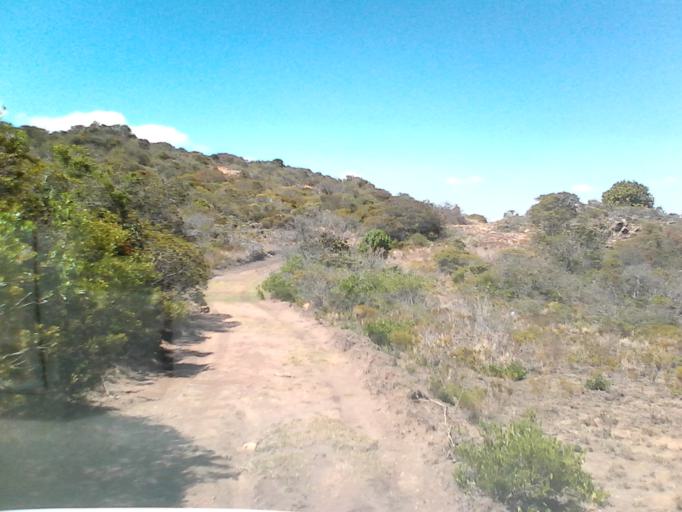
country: CO
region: Boyaca
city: Sachica
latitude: 5.5296
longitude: -73.5448
